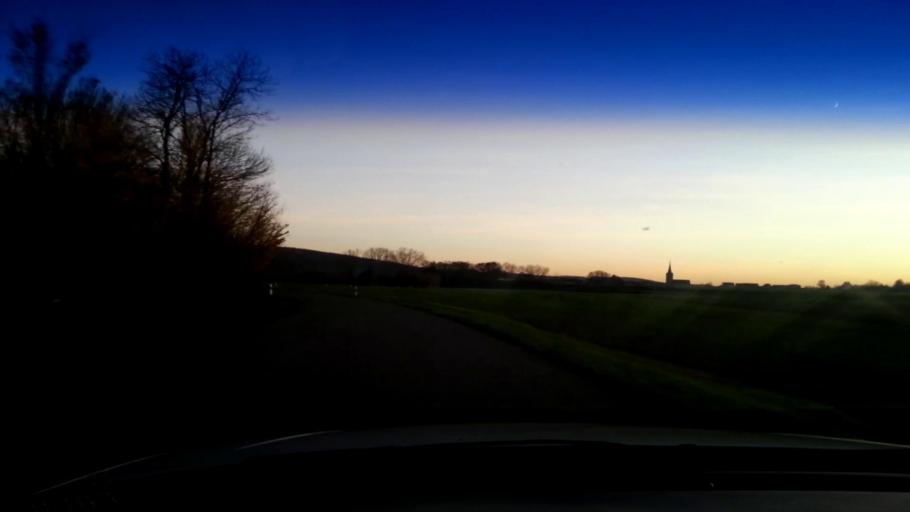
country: DE
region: Bavaria
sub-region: Upper Franconia
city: Rattelsdorf
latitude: 50.0186
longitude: 10.9085
